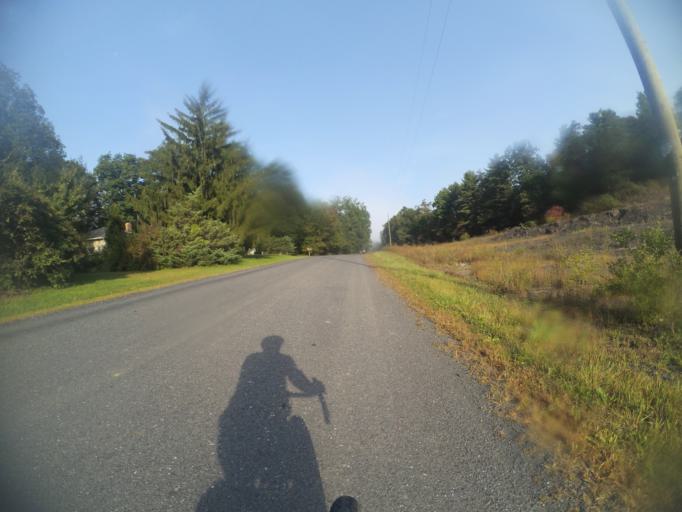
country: US
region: Pennsylvania
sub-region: Centre County
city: Centre Hall
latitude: 40.8705
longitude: -77.6200
